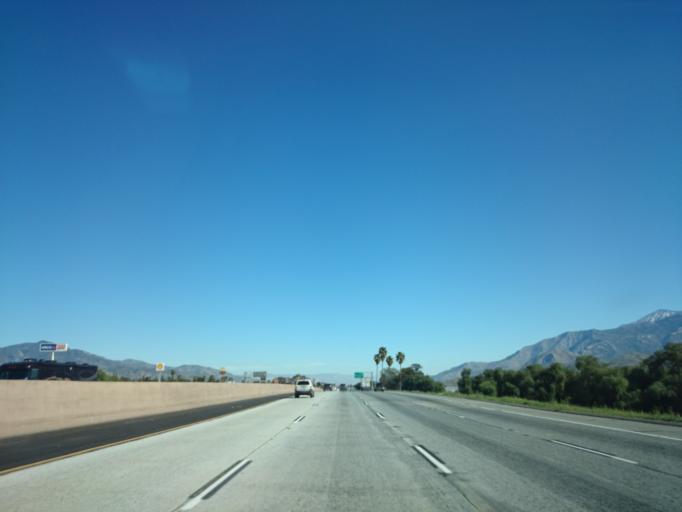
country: US
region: California
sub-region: Riverside County
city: Banning
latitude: 33.9242
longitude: -116.9033
